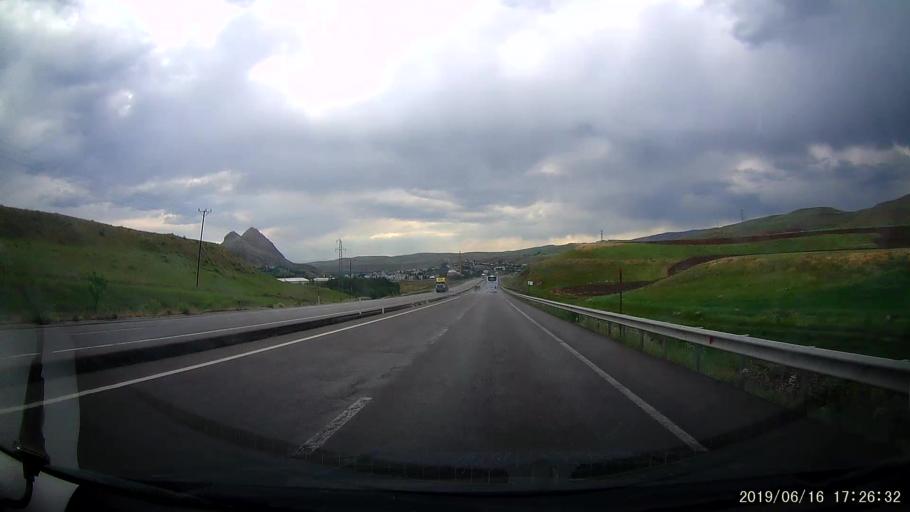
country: TR
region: Erzincan
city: Tercan
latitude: 39.7686
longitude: 40.4103
